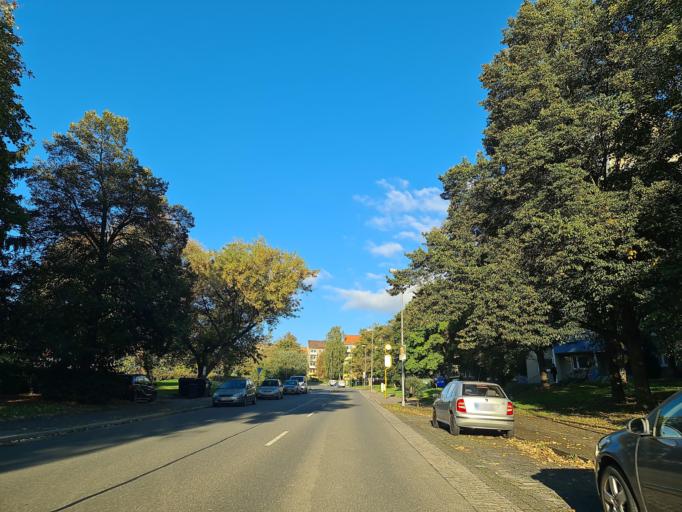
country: DE
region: Thuringia
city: Gera
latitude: 50.8953
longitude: 12.0846
